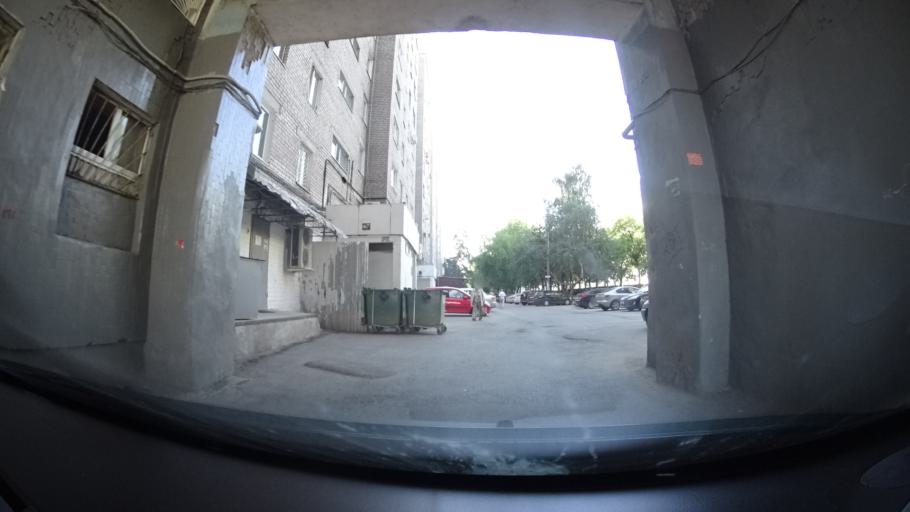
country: RU
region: Bashkortostan
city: Ufa
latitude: 54.7587
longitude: 55.9955
